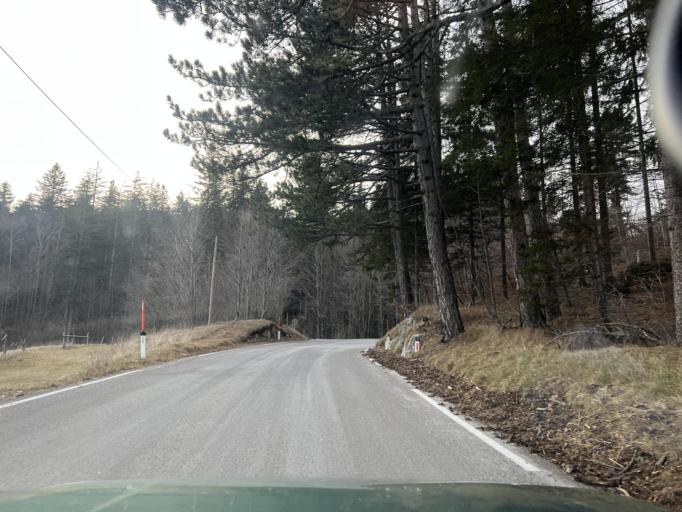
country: SI
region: Nova Gorica
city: Sempas
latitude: 45.9886
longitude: 13.7675
